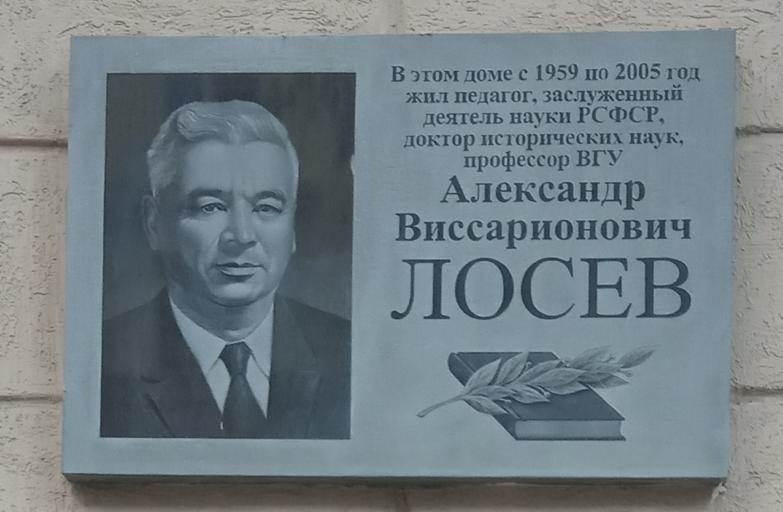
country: RU
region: Voronezj
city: Voronezh
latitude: 51.6654
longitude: 39.2092
